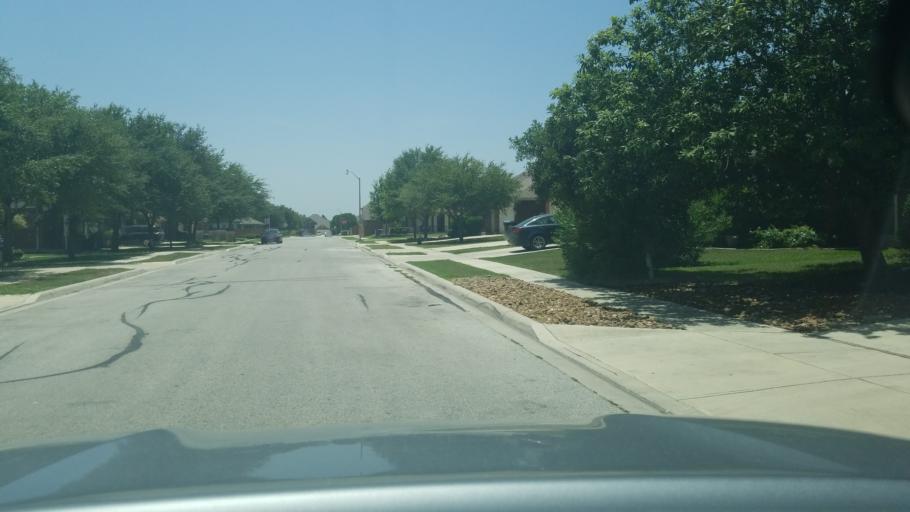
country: US
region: Texas
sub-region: Guadalupe County
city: Cibolo
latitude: 29.5778
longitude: -98.2277
